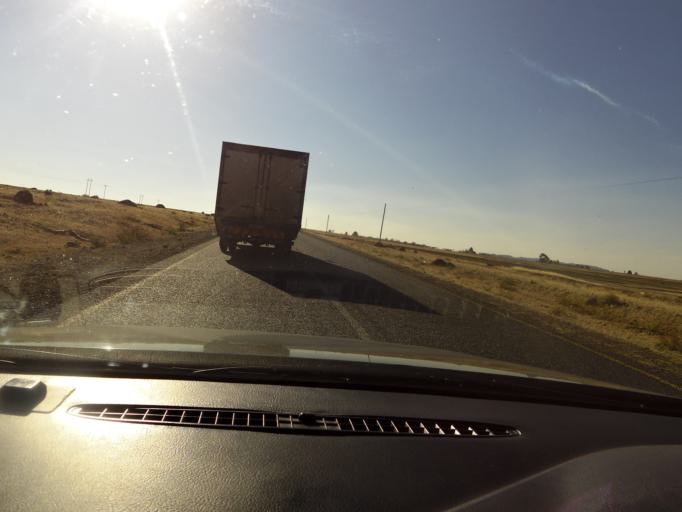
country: LS
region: Mohale's Hoek District
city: Mohale's Hoek
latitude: -30.0010
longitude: 27.3431
